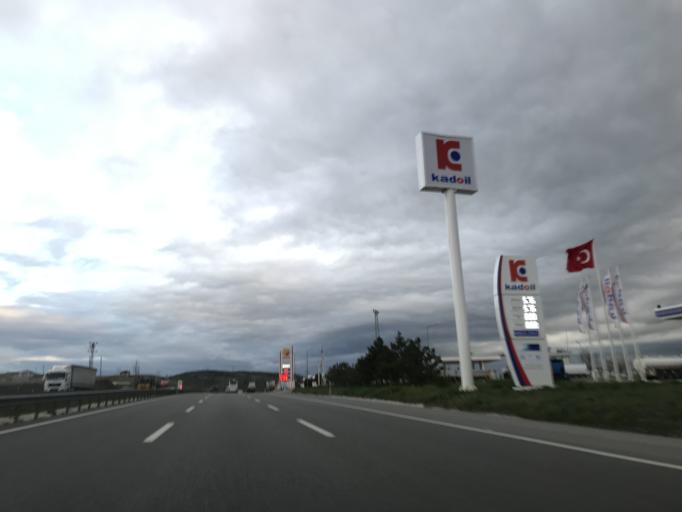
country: TR
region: Ankara
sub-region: Goelbasi
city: Golbasi
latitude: 39.6917
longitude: 32.8173
